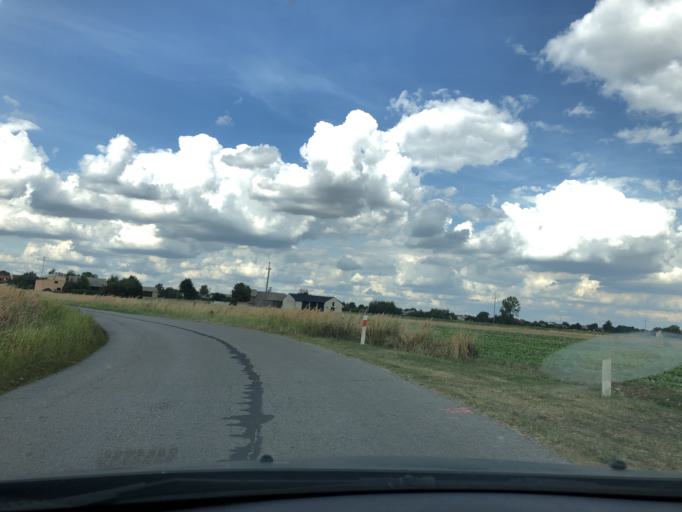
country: PL
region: Lodz Voivodeship
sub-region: Powiat wieruszowski
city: Walichnowy
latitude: 51.2568
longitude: 18.3941
